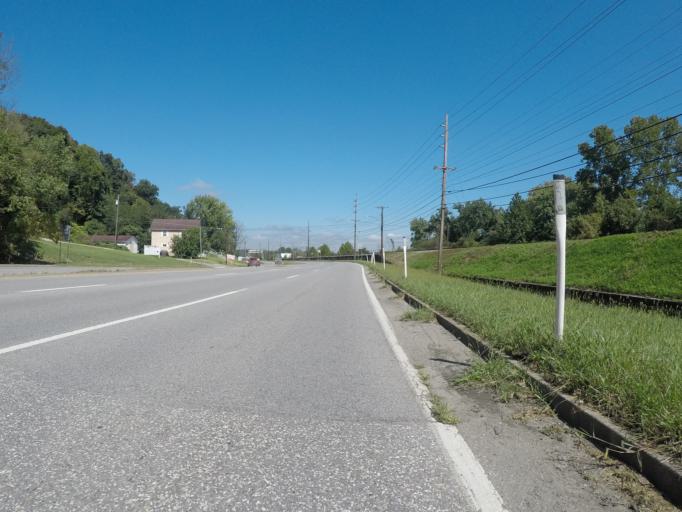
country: US
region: Ohio
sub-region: Lawrence County
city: South Point
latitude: 38.4288
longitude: -82.6032
